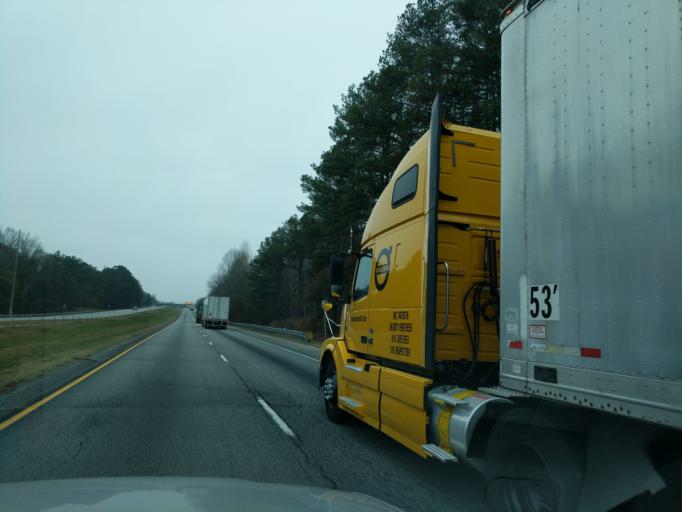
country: US
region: Georgia
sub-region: Franklin County
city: Lavonia
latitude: 34.4278
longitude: -83.1564
